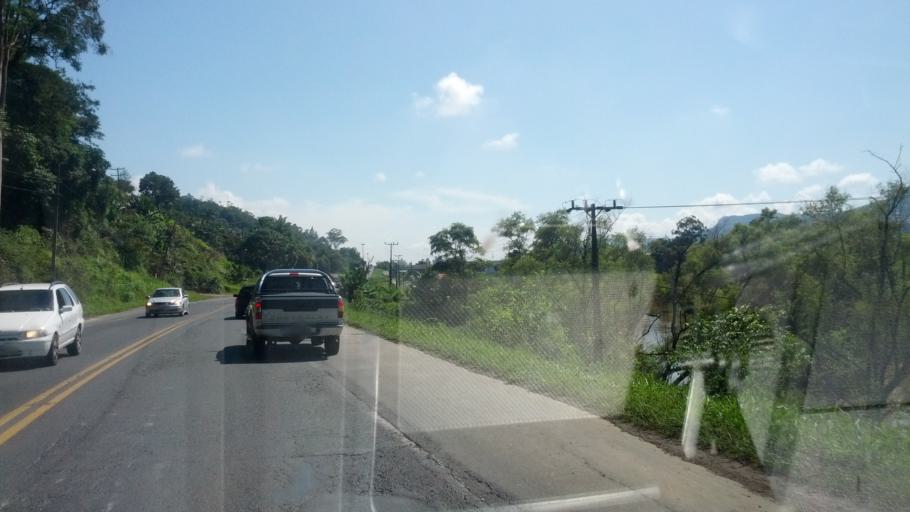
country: BR
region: Santa Catarina
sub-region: Rio Do Sul
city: Rio do Sul
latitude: -27.2230
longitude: -49.6635
